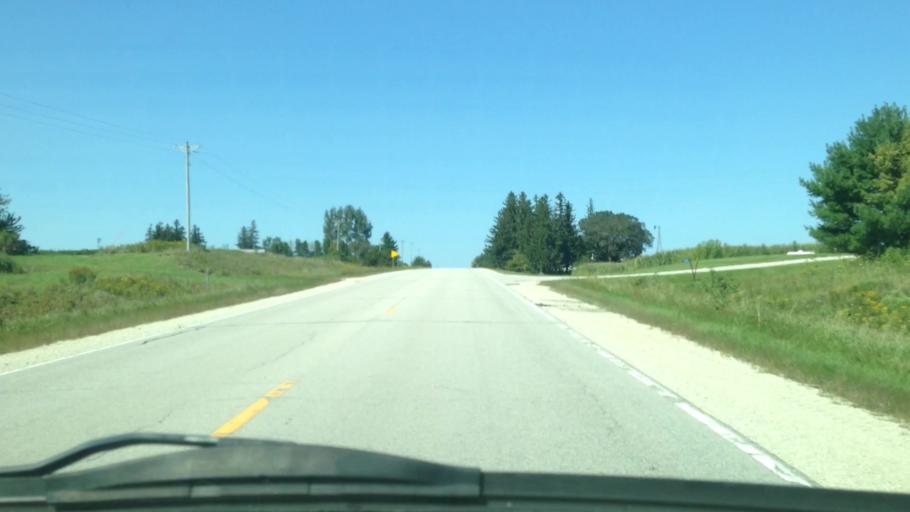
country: US
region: Minnesota
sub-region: Houston County
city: Spring Grove
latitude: 43.6181
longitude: -91.7903
